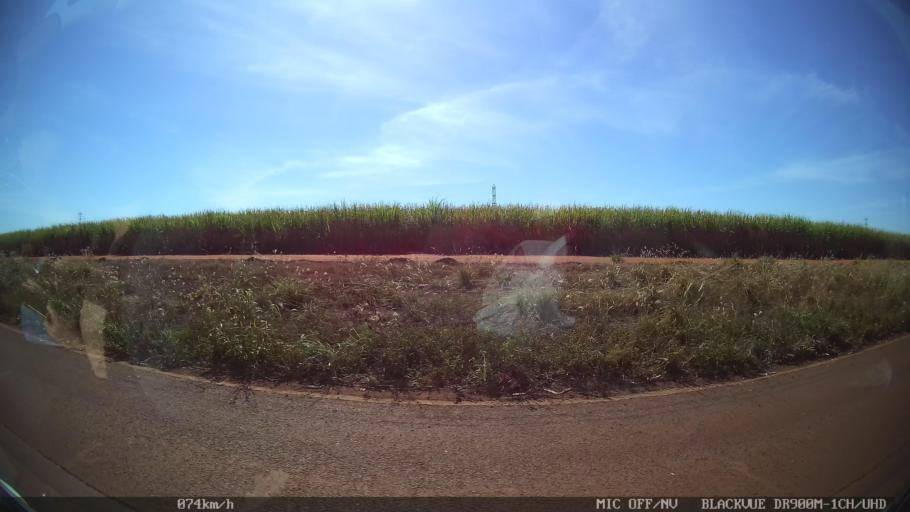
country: BR
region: Sao Paulo
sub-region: Barretos
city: Barretos
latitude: -20.4465
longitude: -48.4386
